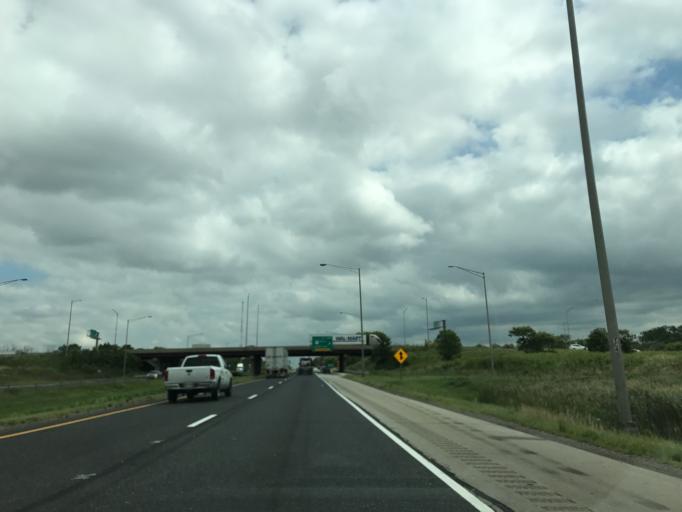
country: US
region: Illinois
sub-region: Will County
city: Rockdale
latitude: 41.5112
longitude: -88.1269
